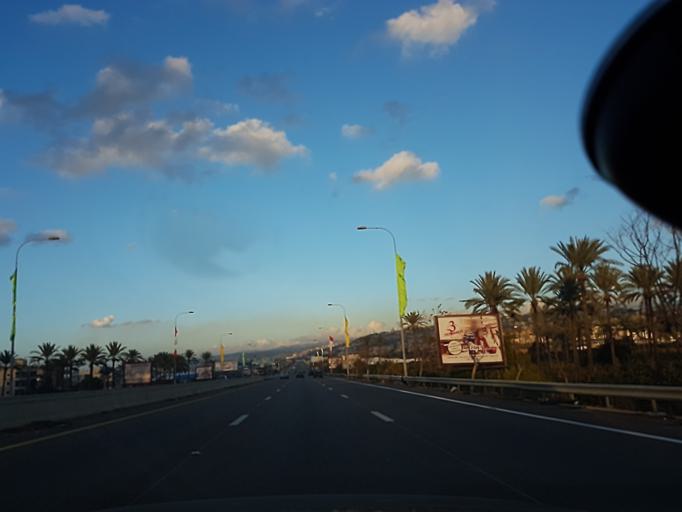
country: LB
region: Liban-Sud
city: Sidon
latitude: 33.5037
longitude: 35.3478
